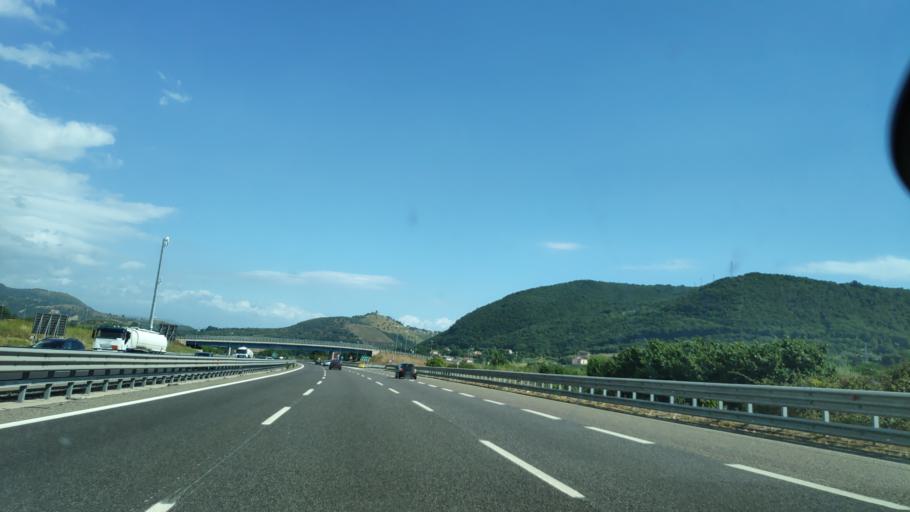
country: IT
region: Campania
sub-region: Provincia di Salerno
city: San Mango Piemonte
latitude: 40.6911
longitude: 14.8366
